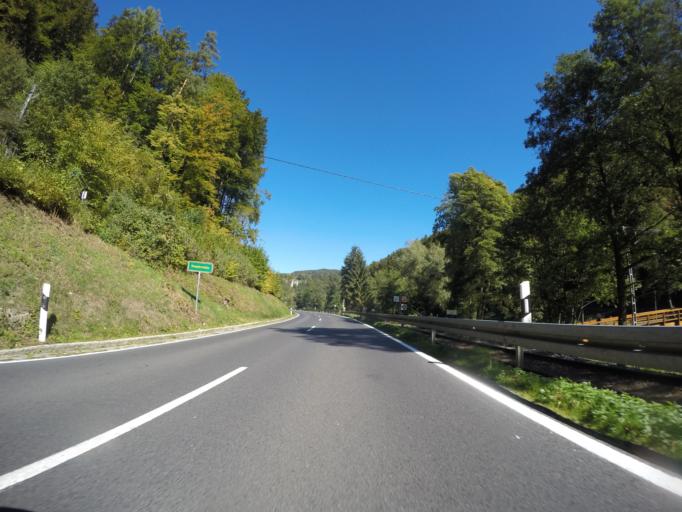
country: DE
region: Bavaria
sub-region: Upper Franconia
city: Gossweinstein
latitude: 49.7716
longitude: 11.3308
